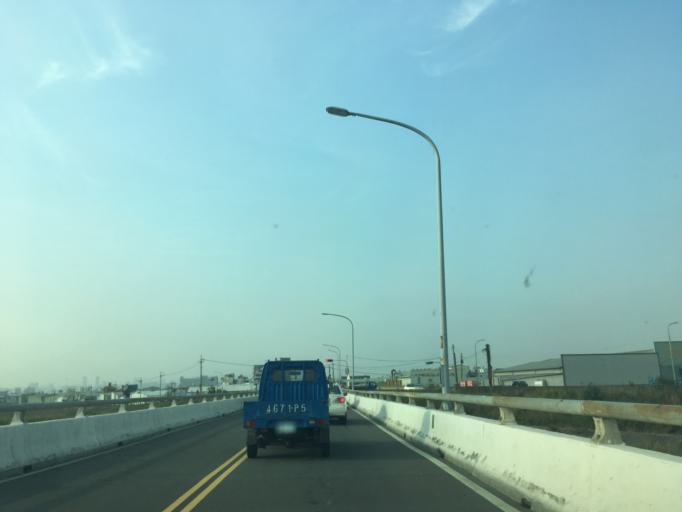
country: TW
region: Taiwan
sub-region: Taichung City
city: Taichung
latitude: 24.0731
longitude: 120.6800
